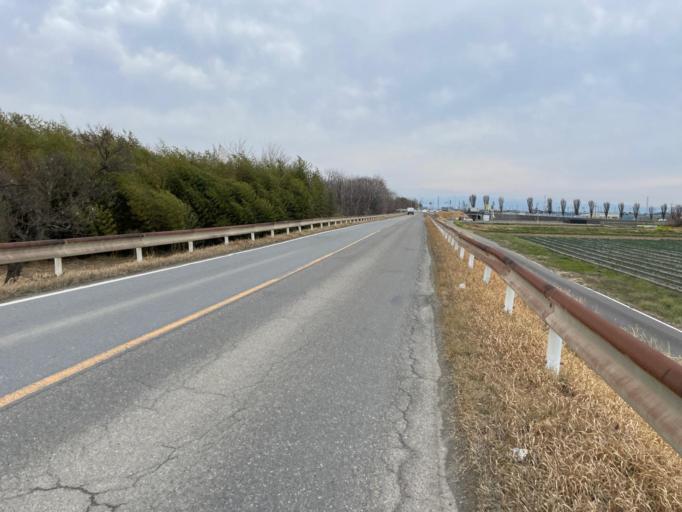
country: JP
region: Gunma
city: Fujioka
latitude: 36.2330
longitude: 139.0981
